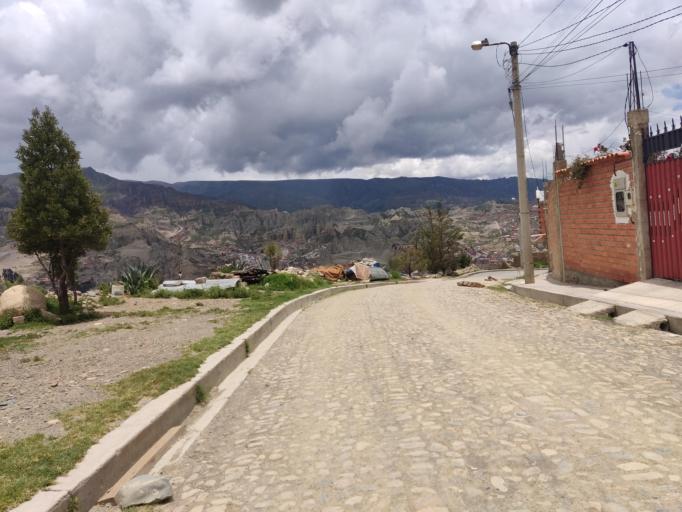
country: BO
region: La Paz
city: La Paz
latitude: -16.5051
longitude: -68.0954
